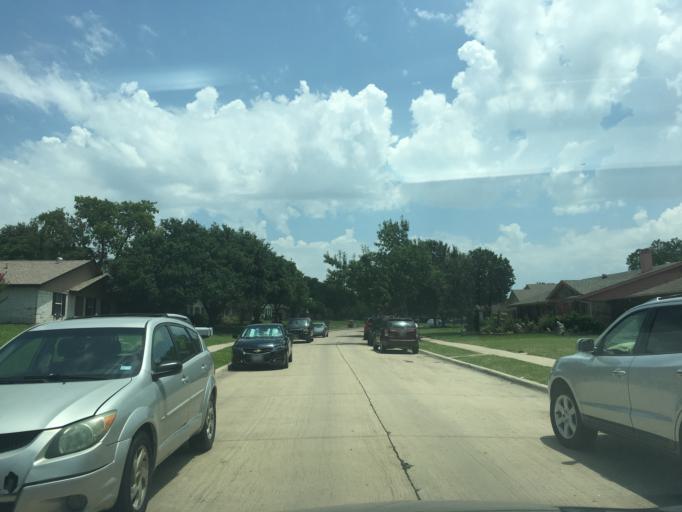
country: US
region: Texas
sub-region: Dallas County
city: Carrollton
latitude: 32.9482
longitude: -96.8806
